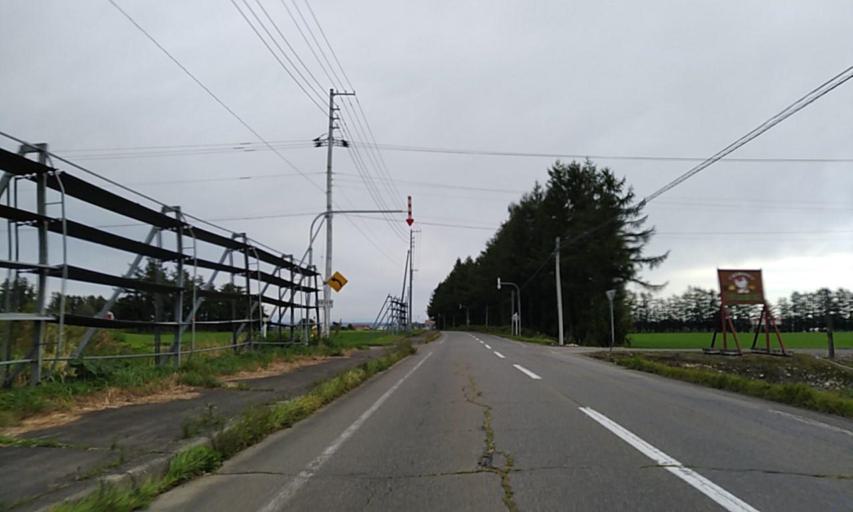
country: JP
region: Hokkaido
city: Obihiro
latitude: 42.8475
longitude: 143.0015
